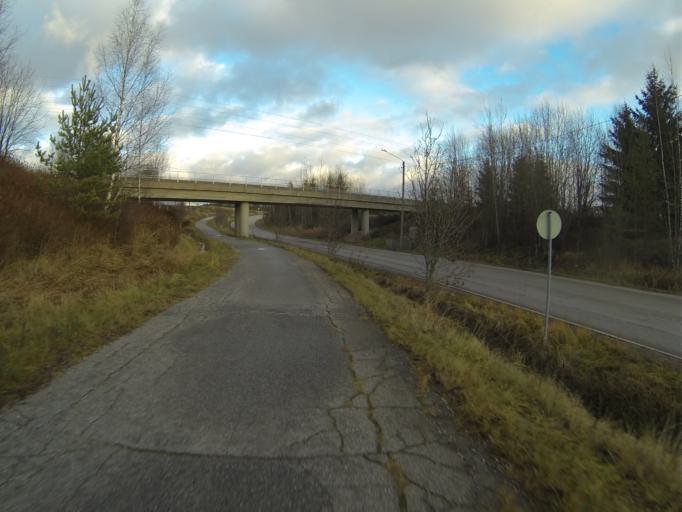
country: FI
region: Varsinais-Suomi
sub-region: Salo
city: Halikko
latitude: 60.3987
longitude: 23.0440
